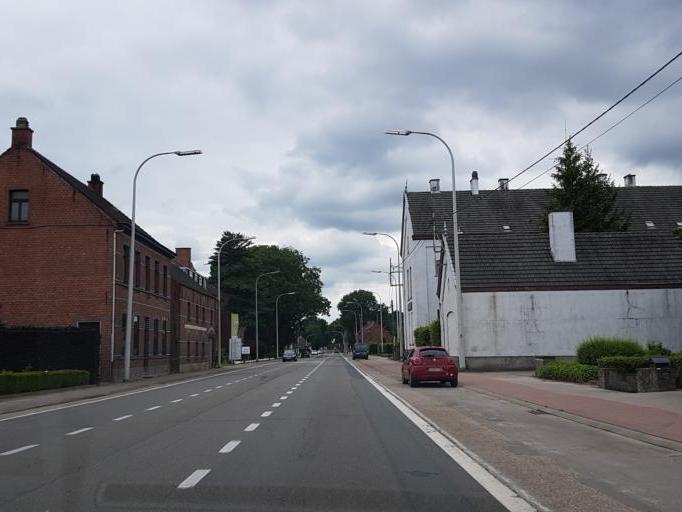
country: BE
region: Flanders
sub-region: Provincie Antwerpen
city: Oostmalle
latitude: 51.2999
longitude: 4.7214
